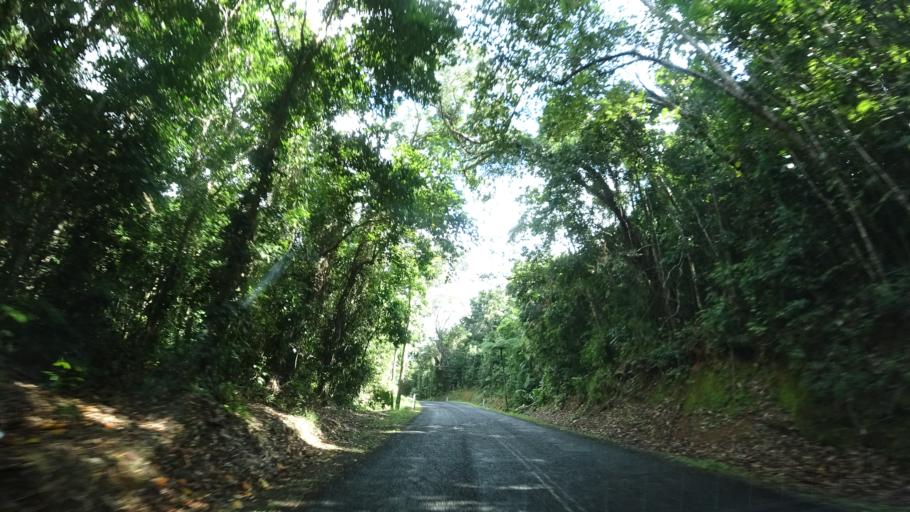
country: AU
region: Queensland
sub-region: Cairns
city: Port Douglas
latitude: -16.1740
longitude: 145.4332
